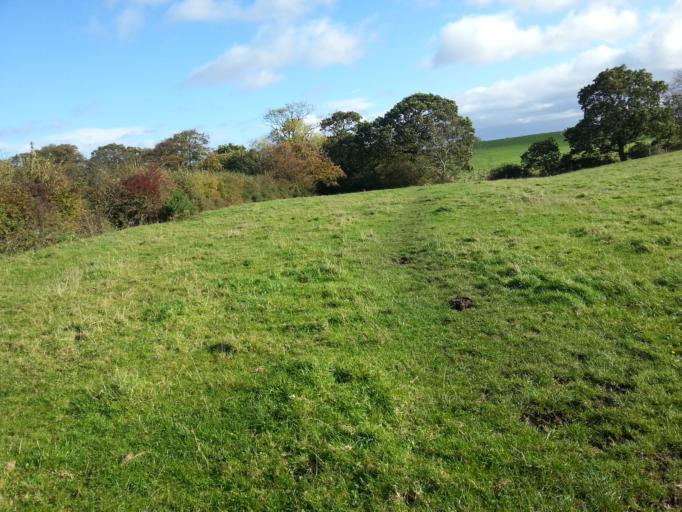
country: GB
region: England
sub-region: Metropolitan Borough of Wirral
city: Heswall
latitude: 53.3515
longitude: -3.1102
